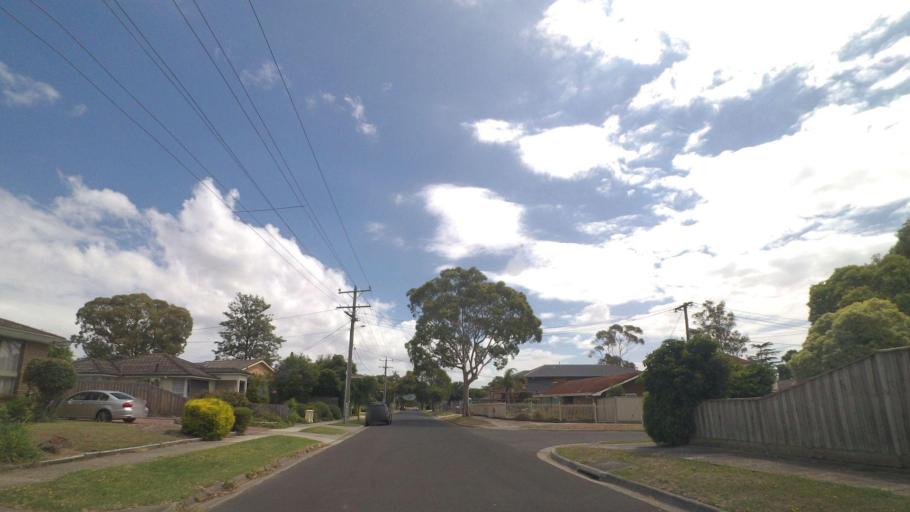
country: AU
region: Victoria
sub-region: Knox
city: Wantirna South
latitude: -37.8845
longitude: 145.2223
